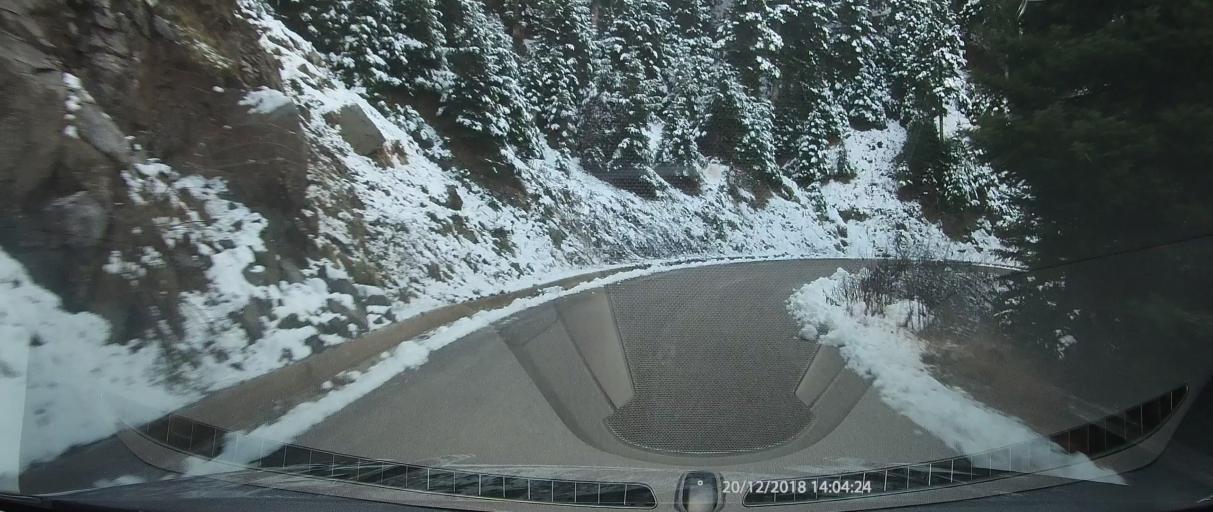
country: GR
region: West Greece
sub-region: Nomos Aitolias kai Akarnanias
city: Thermo
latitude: 38.7431
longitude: 21.6400
